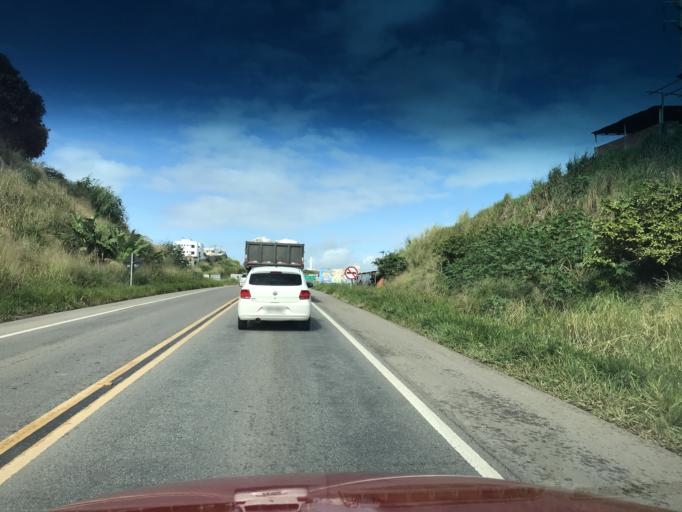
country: BR
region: Bahia
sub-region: Santo Antonio De Jesus
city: Santo Antonio de Jesus
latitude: -12.9581
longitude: -39.2696
